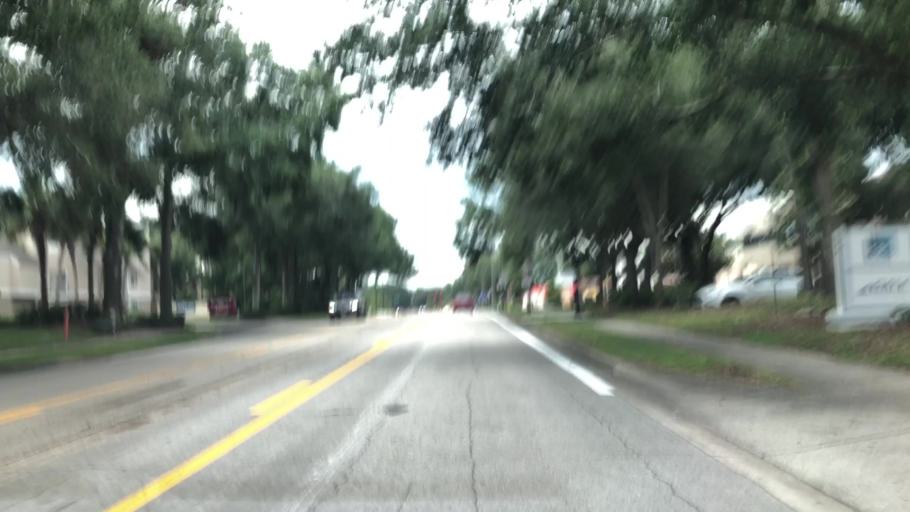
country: US
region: Florida
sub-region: Seminole County
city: Altamonte Springs
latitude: 28.6650
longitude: -81.3936
